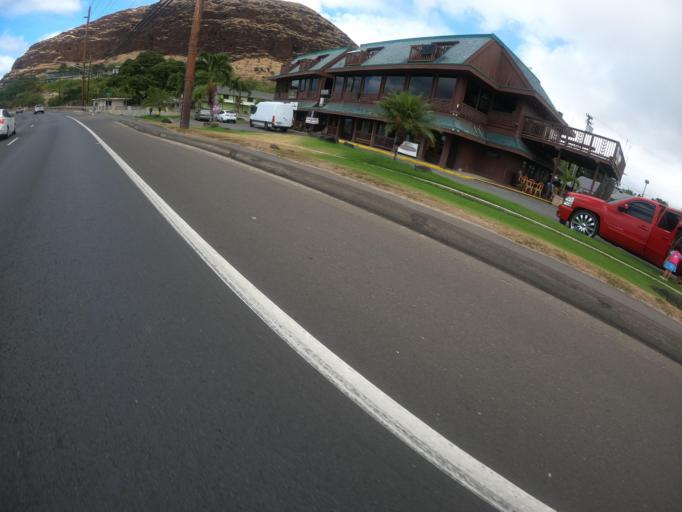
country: US
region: Hawaii
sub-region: Honolulu County
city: Ma'ili
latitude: 21.4277
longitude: -158.1788
